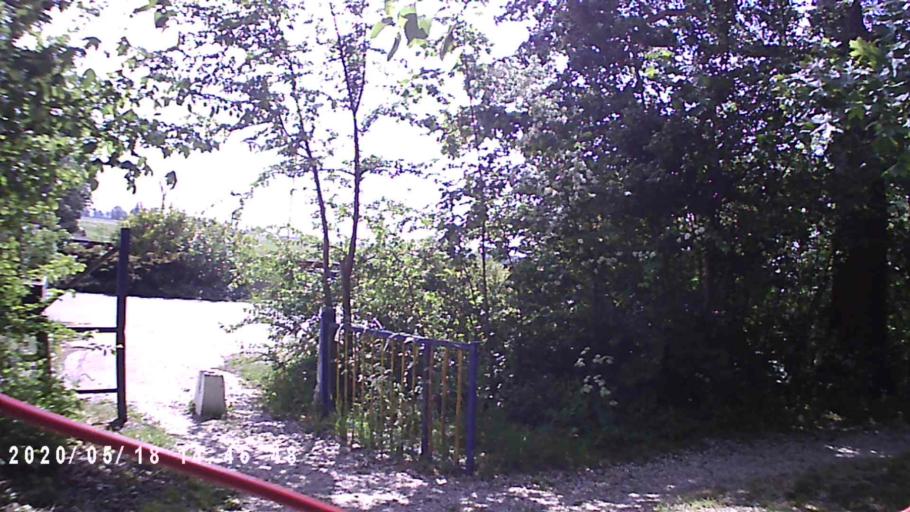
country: NL
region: Groningen
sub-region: Gemeente Winsum
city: Winsum
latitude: 53.3330
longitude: 6.5074
